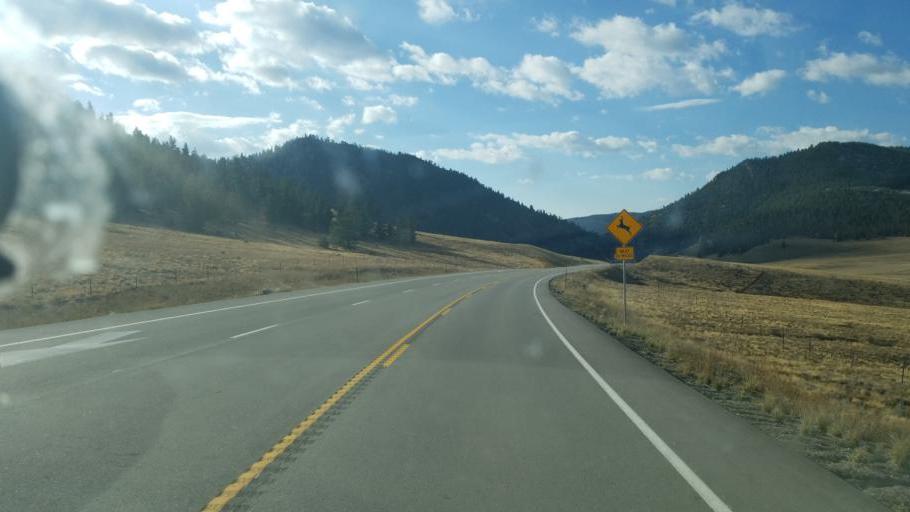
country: US
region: Colorado
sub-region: Chaffee County
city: Buena Vista
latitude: 38.8729
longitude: -105.9843
